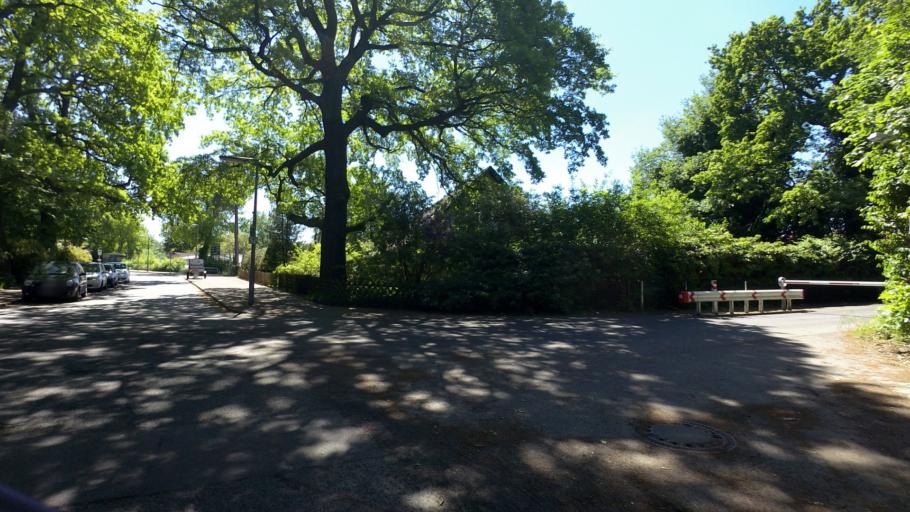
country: DE
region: Berlin
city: Siemensstadt
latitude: 52.5508
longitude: 13.2691
